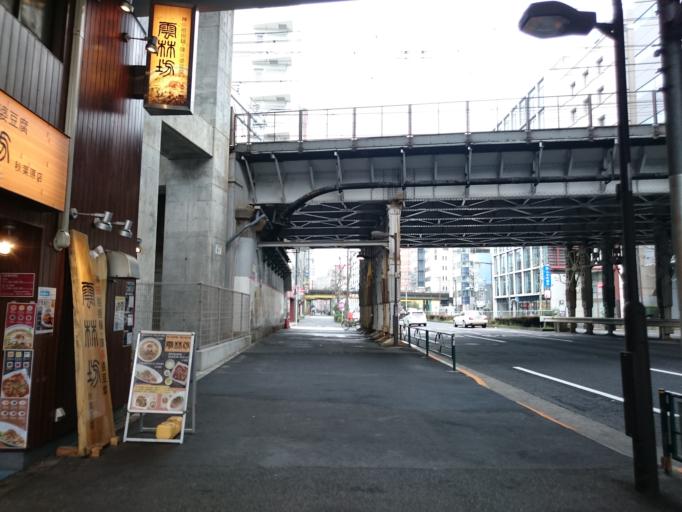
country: JP
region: Tokyo
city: Tokyo
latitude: 35.6955
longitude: 139.7731
